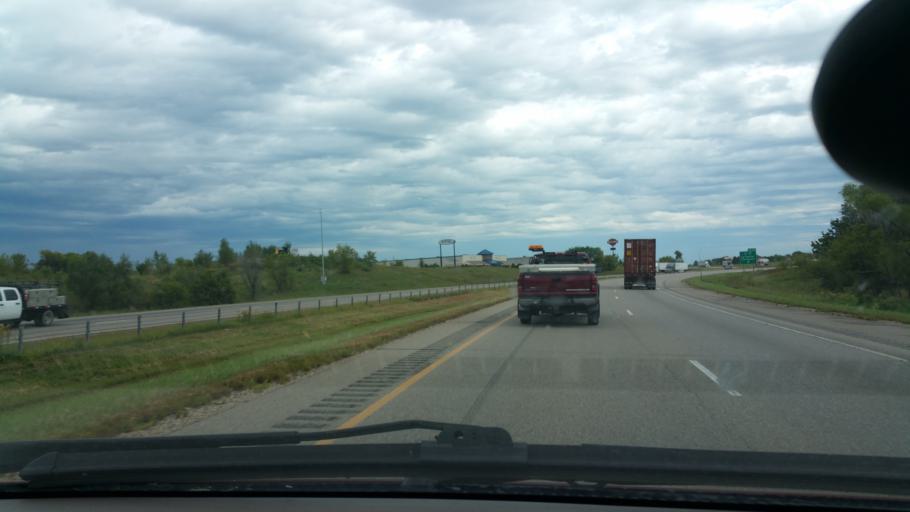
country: US
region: Minnesota
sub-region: Rice County
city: Faribault
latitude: 44.3160
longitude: -93.3076
